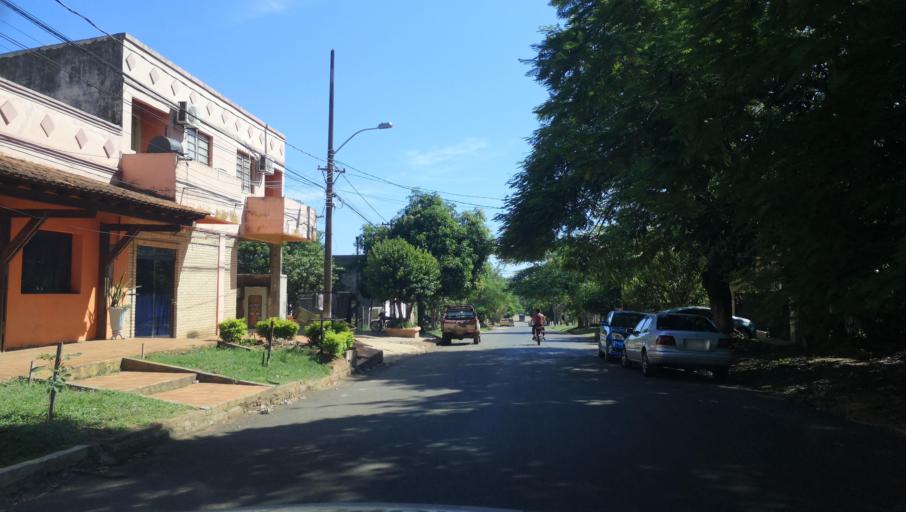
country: PY
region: Misiones
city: Santa Maria
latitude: -26.8855
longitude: -57.0241
